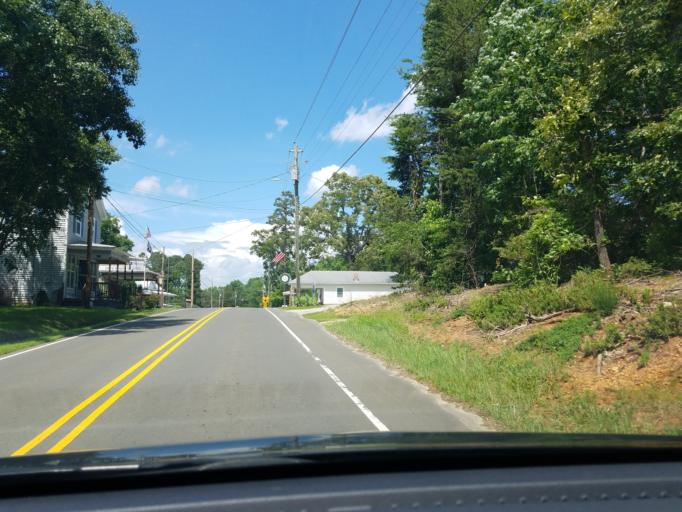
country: US
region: North Carolina
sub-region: Granville County
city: Butner
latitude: 36.1644
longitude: -78.8785
